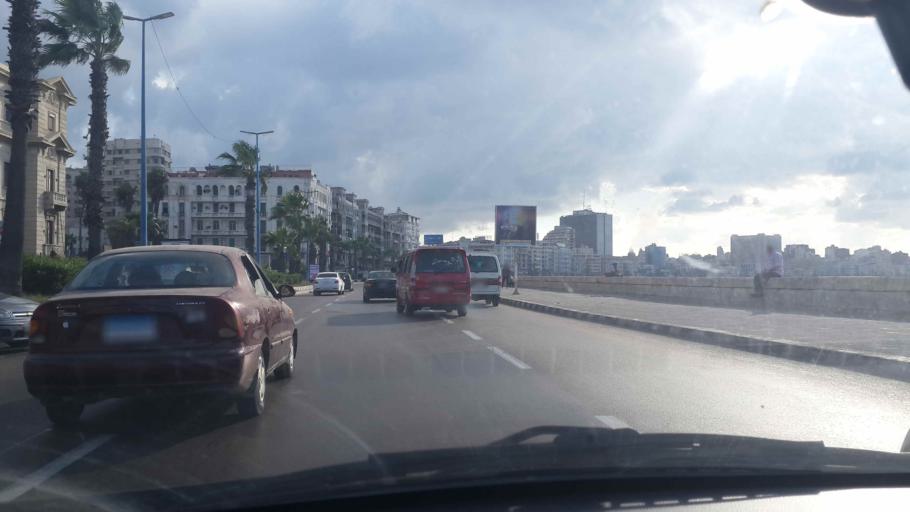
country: EG
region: Alexandria
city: Alexandria
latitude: 31.2046
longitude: 29.9038
